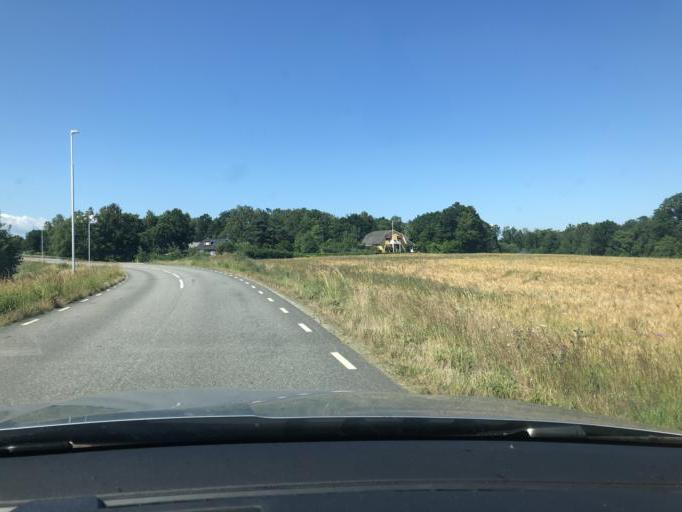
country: SE
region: Blekinge
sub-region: Karlshamns Kommun
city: Morrum
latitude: 56.1687
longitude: 14.6817
